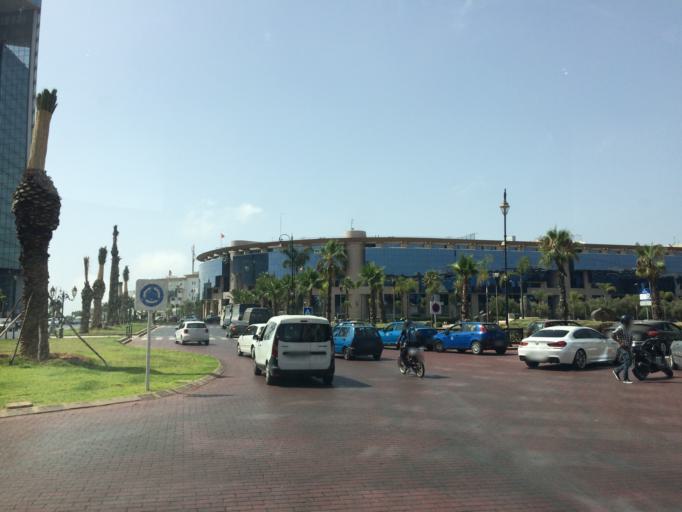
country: MA
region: Rabat-Sale-Zemmour-Zaer
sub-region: Skhirate-Temara
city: Temara
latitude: 33.9576
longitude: -6.8692
